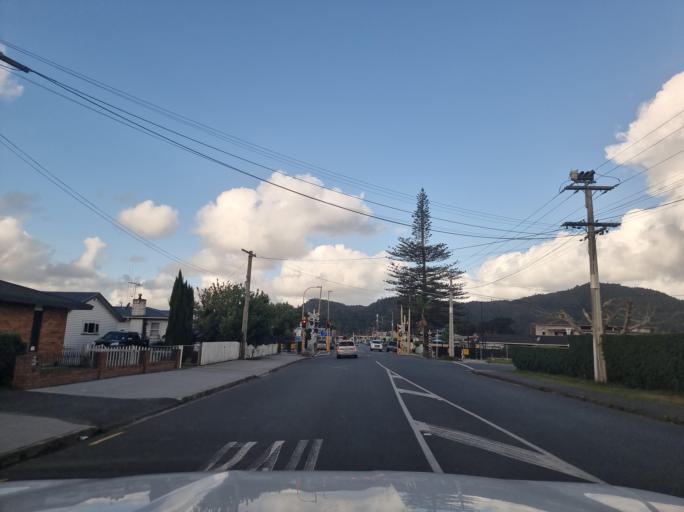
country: NZ
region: Northland
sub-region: Whangarei
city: Whangarei
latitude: -35.7092
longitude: 174.3181
